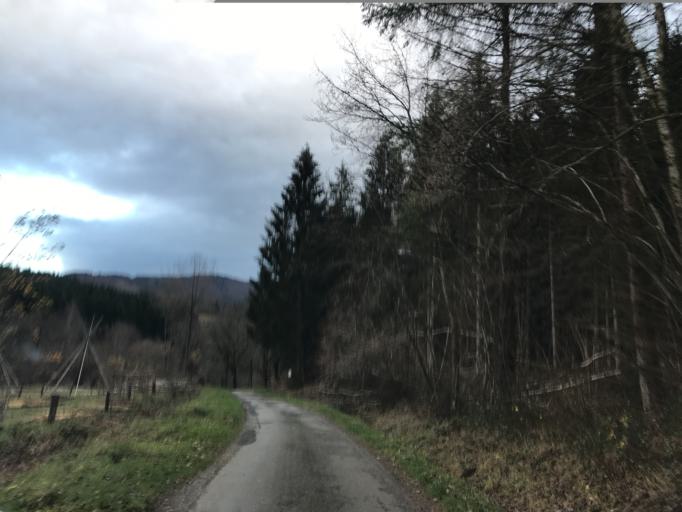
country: FR
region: Auvergne
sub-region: Departement du Puy-de-Dome
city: Celles-sur-Durolle
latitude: 45.8387
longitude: 3.6637
